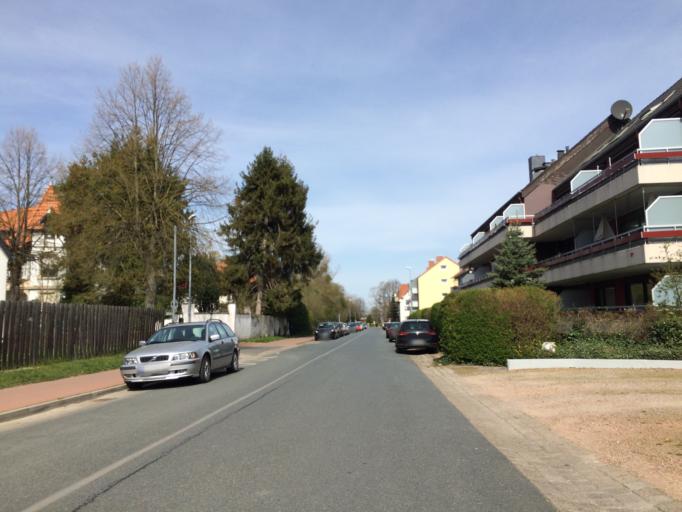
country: DE
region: Lower Saxony
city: Gehrden
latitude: 52.3180
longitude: 9.5982
